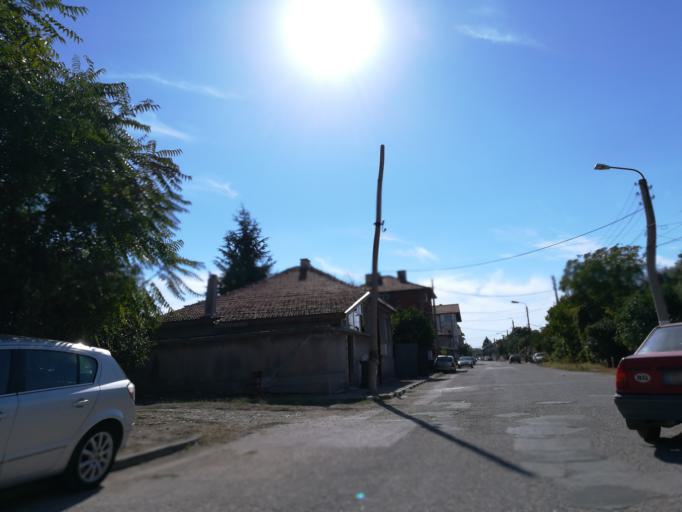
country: BG
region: Stara Zagora
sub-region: Obshtina Chirpan
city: Chirpan
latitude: 42.0942
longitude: 25.2298
